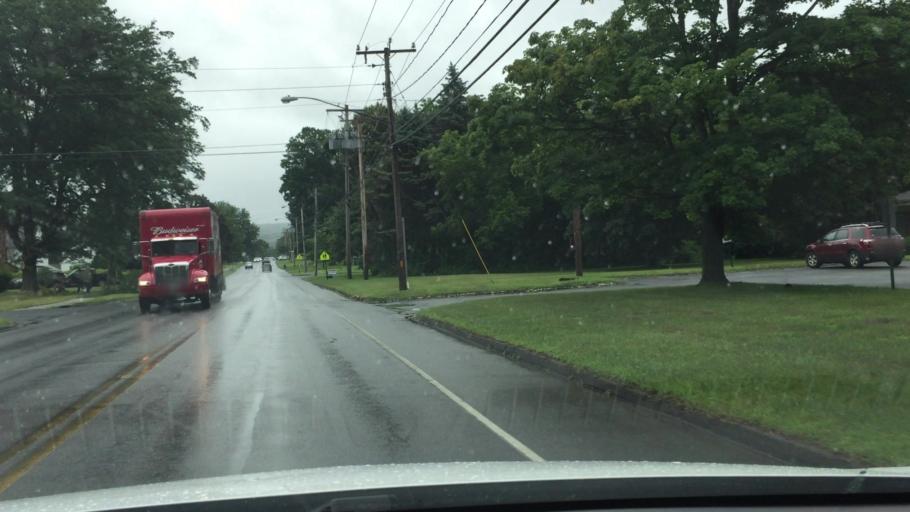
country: US
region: Massachusetts
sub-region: Berkshire County
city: Pittsfield
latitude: 42.4323
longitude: -73.2133
